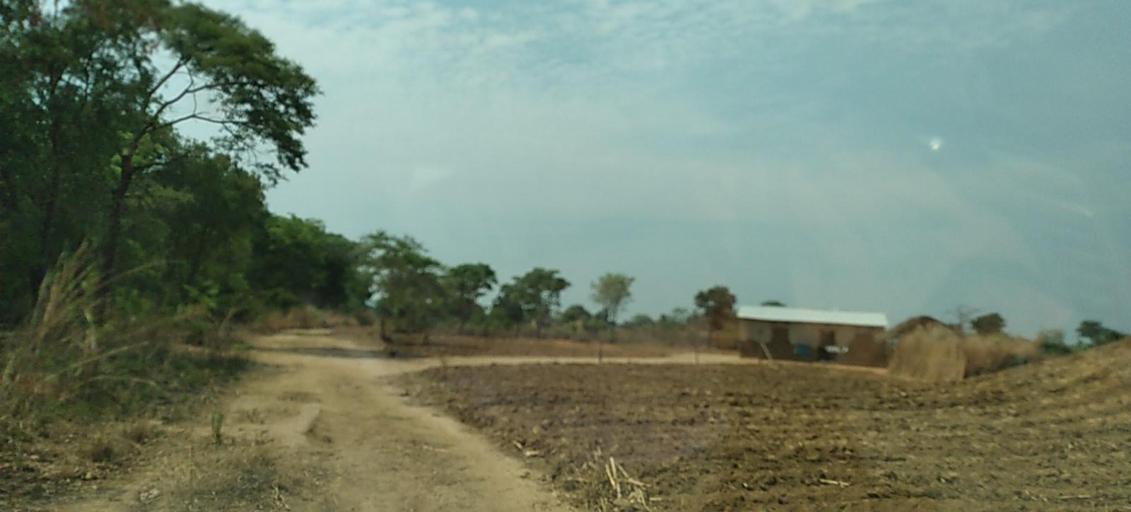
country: ZM
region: Copperbelt
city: Kalulushi
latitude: -12.8960
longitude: 28.0829
